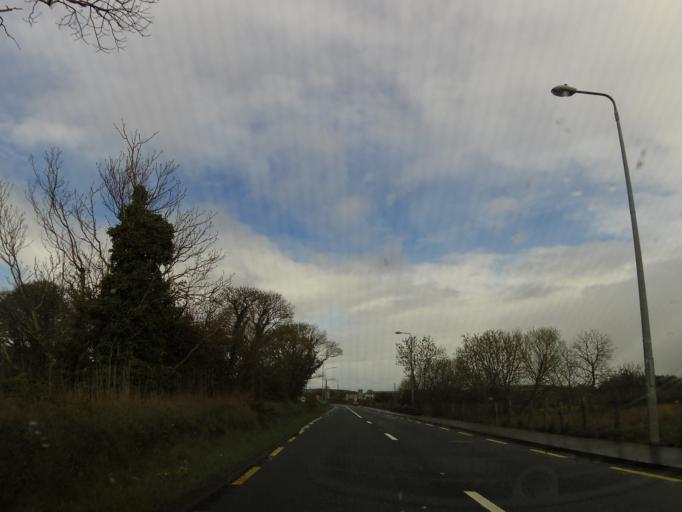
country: IE
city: Ballisodare
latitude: 54.2049
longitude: -8.5035
